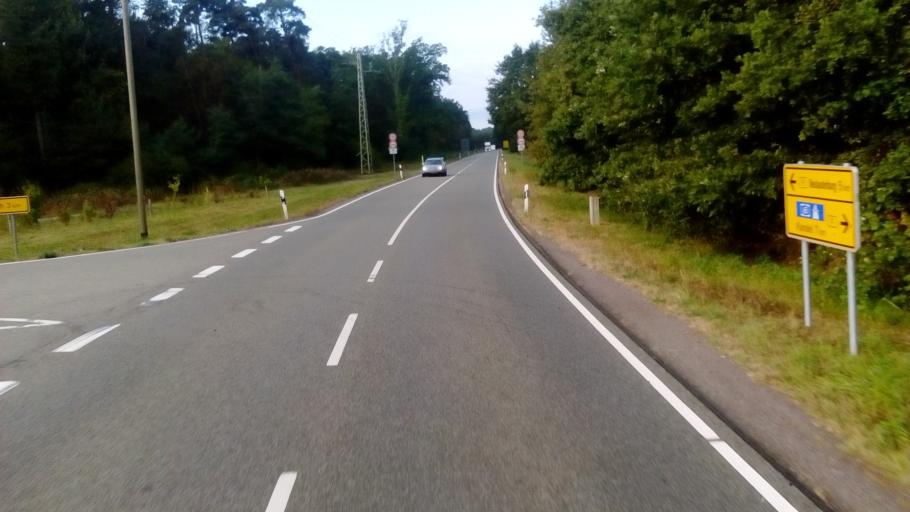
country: DE
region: Rheinland-Pfalz
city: Hagenbach
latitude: 49.0244
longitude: 8.1993
